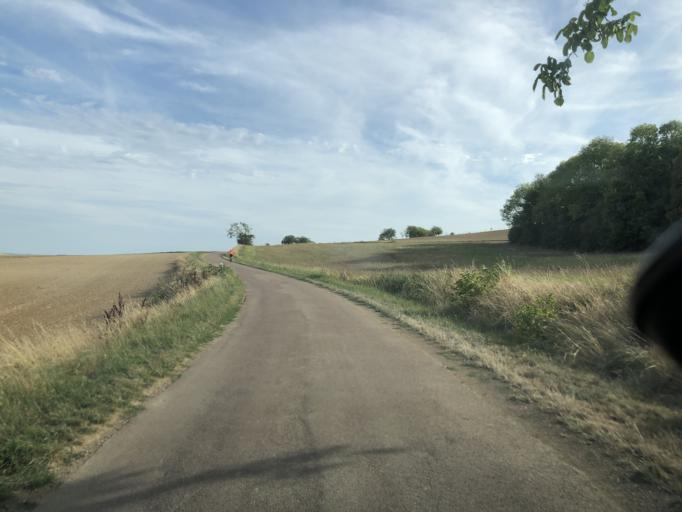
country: FR
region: Bourgogne
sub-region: Departement de l'Yonne
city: Joigny
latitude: 47.9383
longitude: 3.3874
